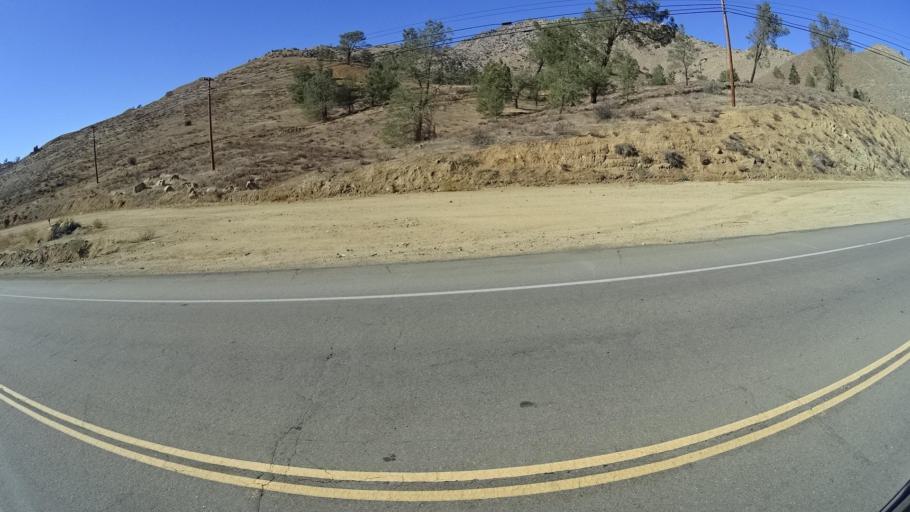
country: US
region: California
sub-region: Kern County
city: Wofford Heights
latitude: 35.7240
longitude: -118.4325
